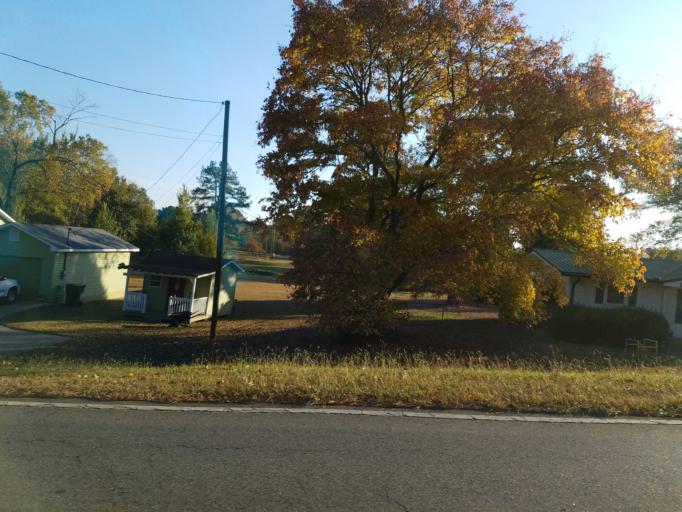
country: US
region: Georgia
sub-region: Bartow County
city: Euharlee
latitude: 34.2389
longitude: -84.9492
